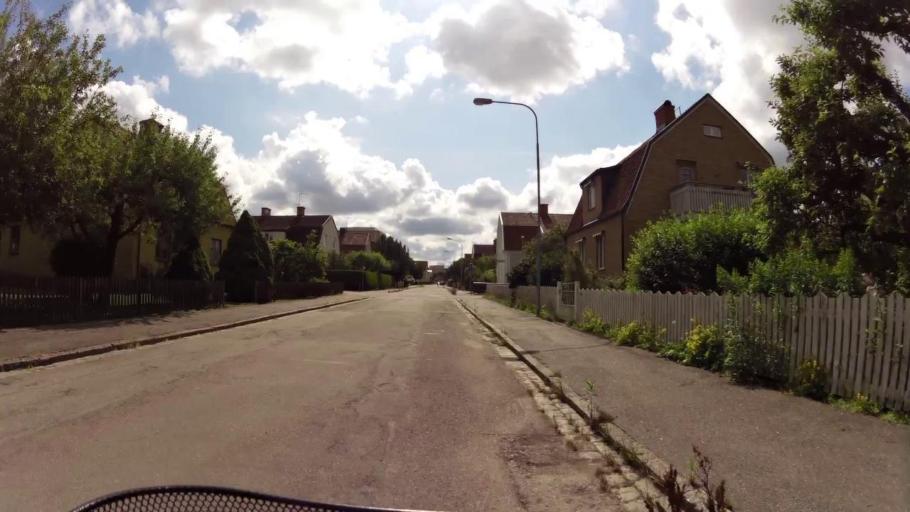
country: SE
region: OEstergoetland
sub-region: Linkopings Kommun
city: Linkoping
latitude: 58.4061
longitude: 15.6397
